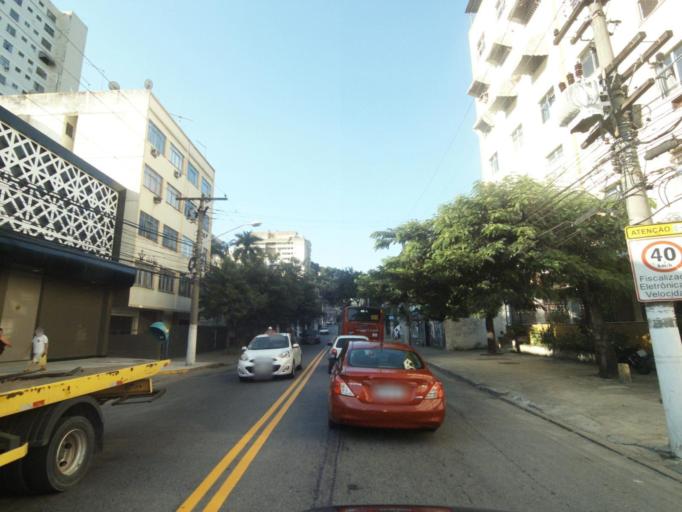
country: BR
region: Rio de Janeiro
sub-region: Niteroi
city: Niteroi
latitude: -22.8925
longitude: -43.0989
